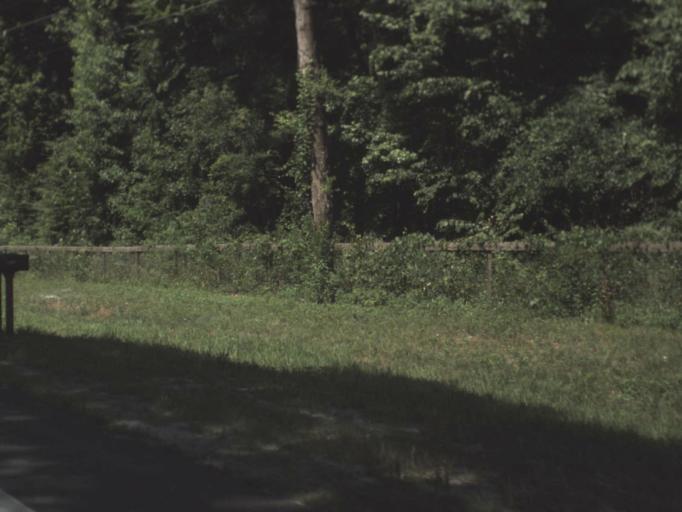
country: US
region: Florida
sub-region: Alachua County
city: Archer
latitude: 29.5313
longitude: -82.4037
